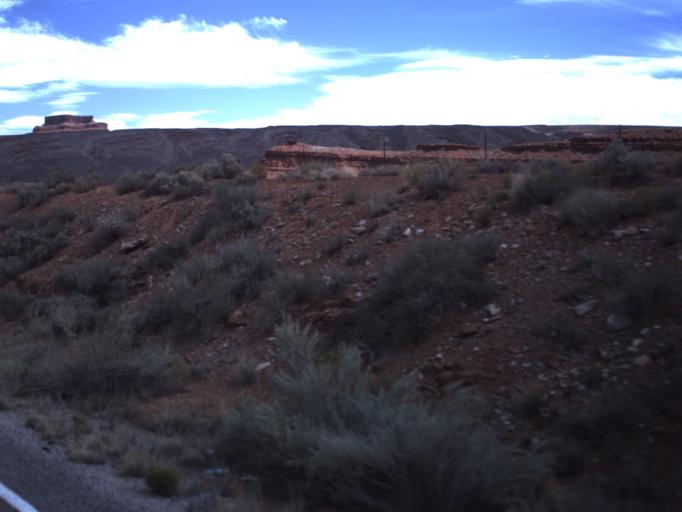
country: US
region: Utah
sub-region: San Juan County
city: Blanding
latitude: 37.2177
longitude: -109.8312
